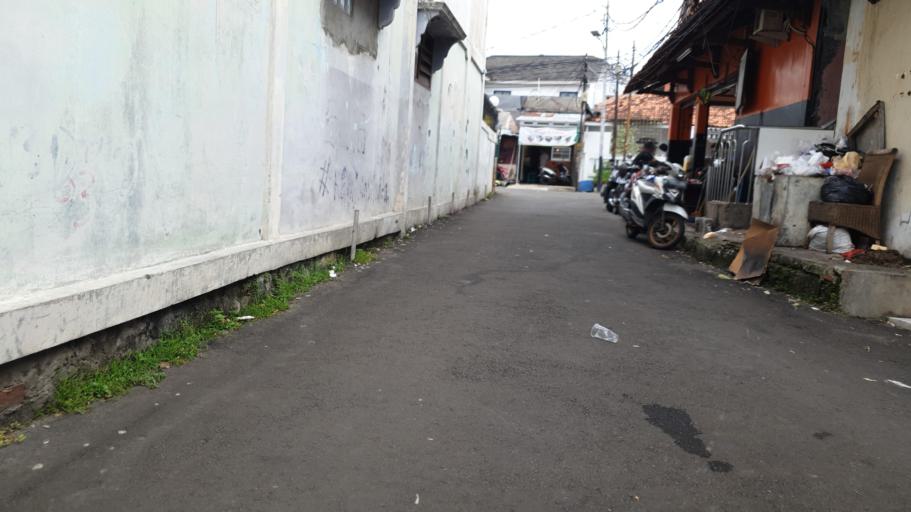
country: ID
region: Jakarta Raya
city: Jakarta
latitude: -6.2653
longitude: 106.7918
